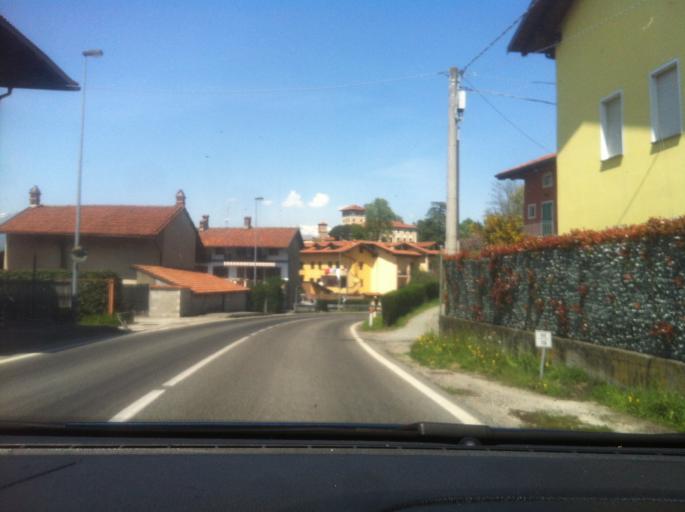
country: IT
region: Piedmont
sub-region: Provincia di Torino
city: Mercenasco
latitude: 45.3521
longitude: 7.8829
